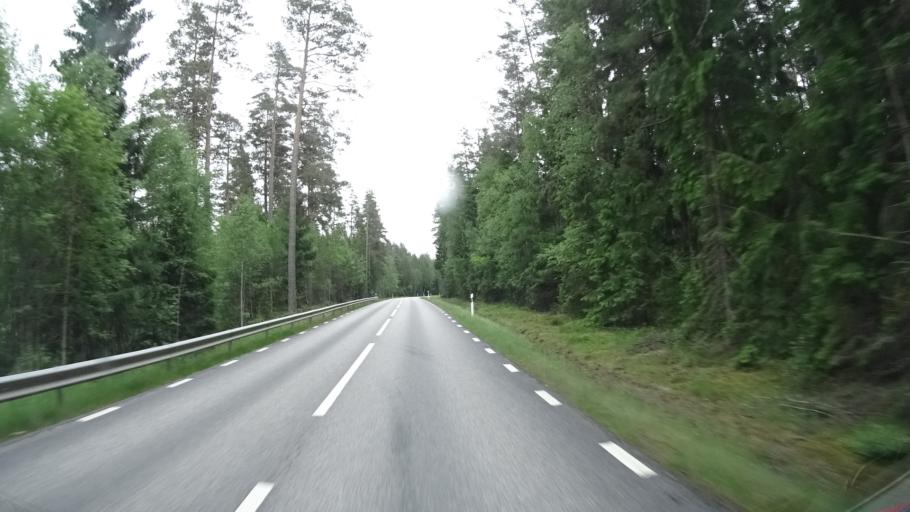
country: SE
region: Joenkoeping
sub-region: Eksjo Kommun
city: Mariannelund
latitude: 57.5705
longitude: 15.7025
